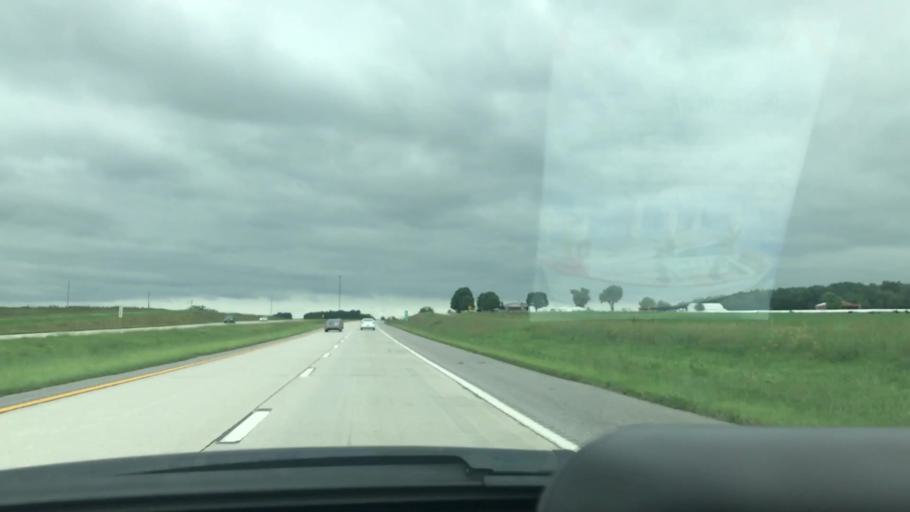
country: US
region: Missouri
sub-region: Greene County
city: Fair Grove
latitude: 37.4418
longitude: -93.1443
